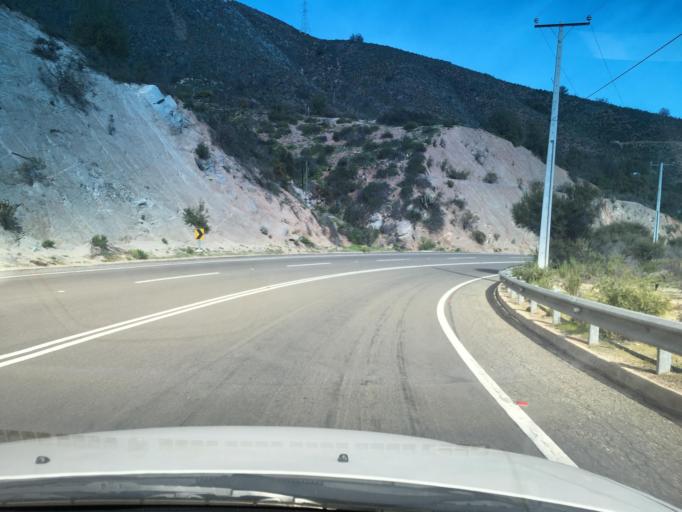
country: CL
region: Valparaiso
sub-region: Provincia de San Felipe
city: Llaillay
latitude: -33.0636
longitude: -71.0249
